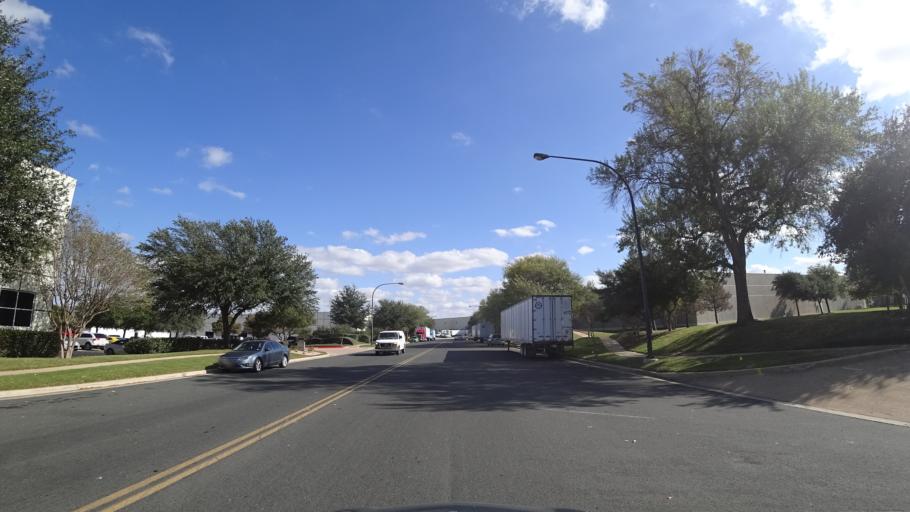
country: US
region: Texas
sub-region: Travis County
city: Wells Branch
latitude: 30.4589
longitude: -97.6733
